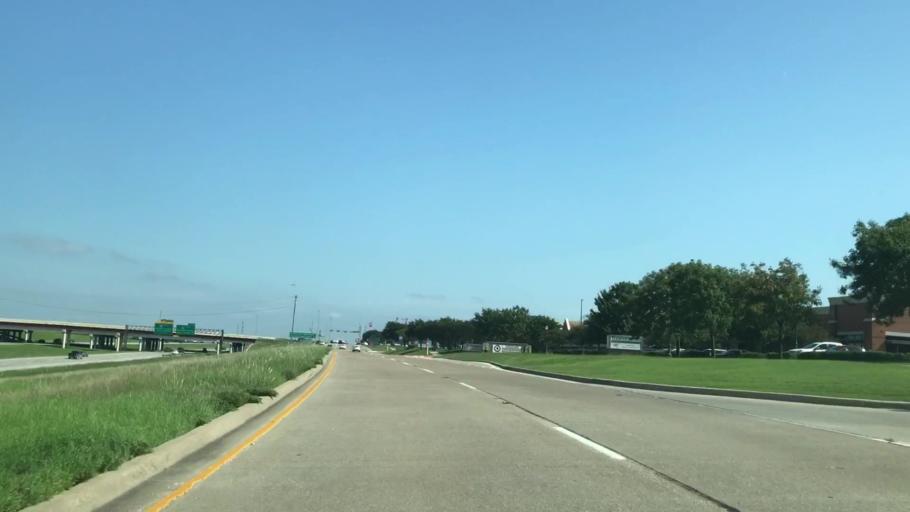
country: US
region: Texas
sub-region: Dallas County
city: Coppell
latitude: 32.9155
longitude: -96.9628
